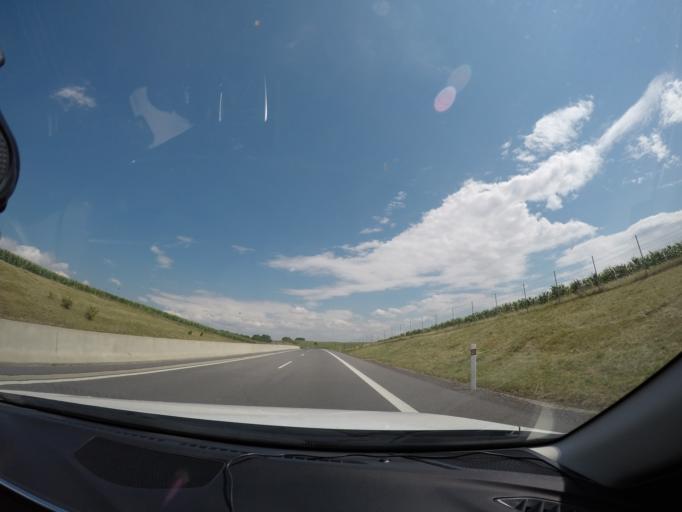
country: SK
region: Nitriansky
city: Zlate Moravce
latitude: 48.3462
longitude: 18.3891
